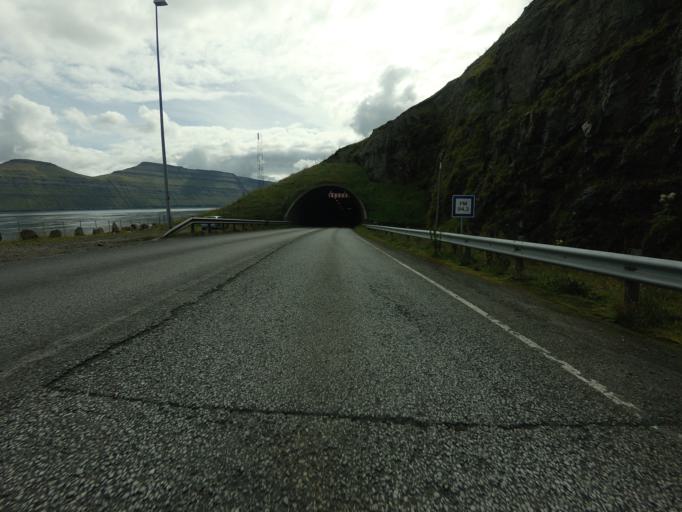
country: FO
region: Eysturoy
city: Eystur
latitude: 62.2076
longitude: -6.6822
